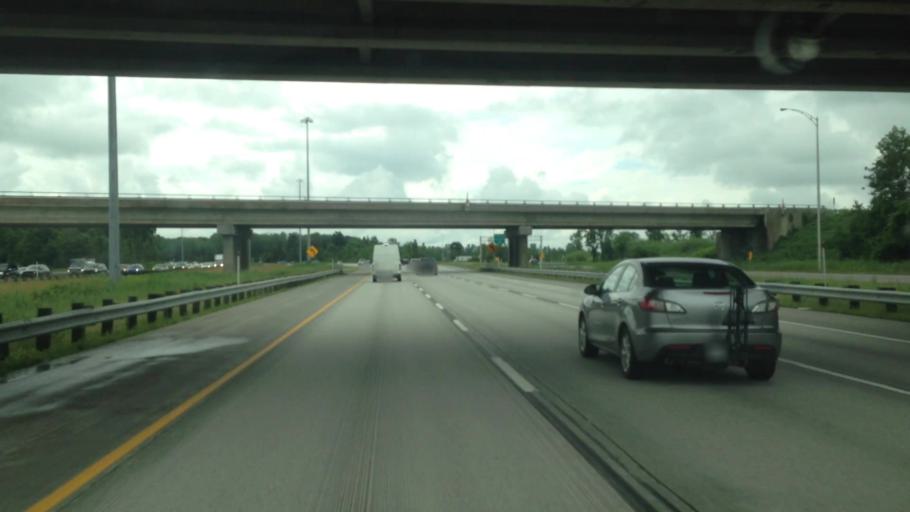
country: CA
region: Quebec
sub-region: Laurentides
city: Saint-Jerome
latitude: 45.7209
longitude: -73.9708
